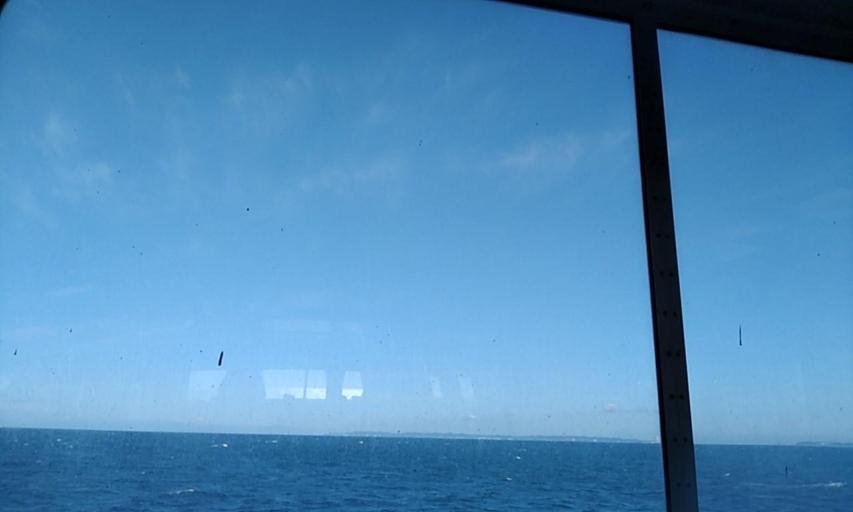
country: JP
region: Aichi
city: Toyohama
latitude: 34.5817
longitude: 136.9932
